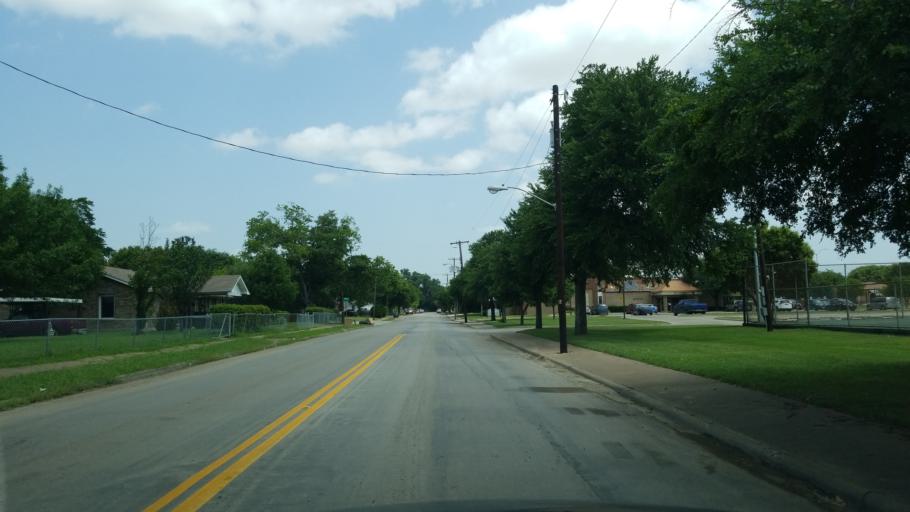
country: US
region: Texas
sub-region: Dallas County
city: Cockrell Hill
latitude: 32.7793
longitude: -96.9095
